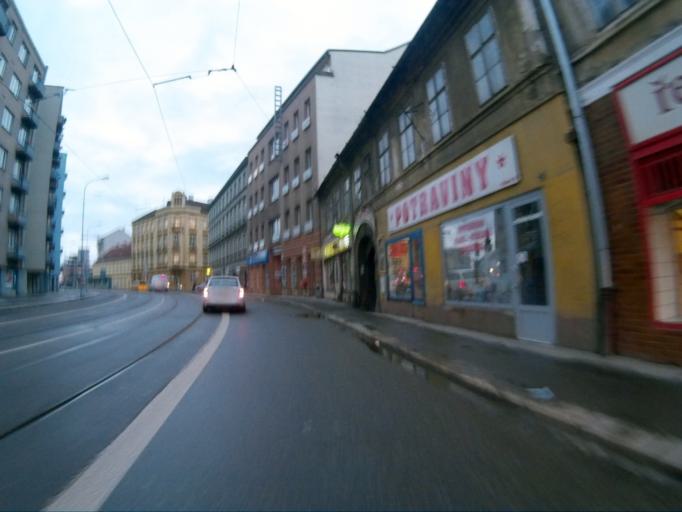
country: CZ
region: South Moravian
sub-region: Mesto Brno
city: Brno
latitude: 49.1888
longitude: 16.5943
